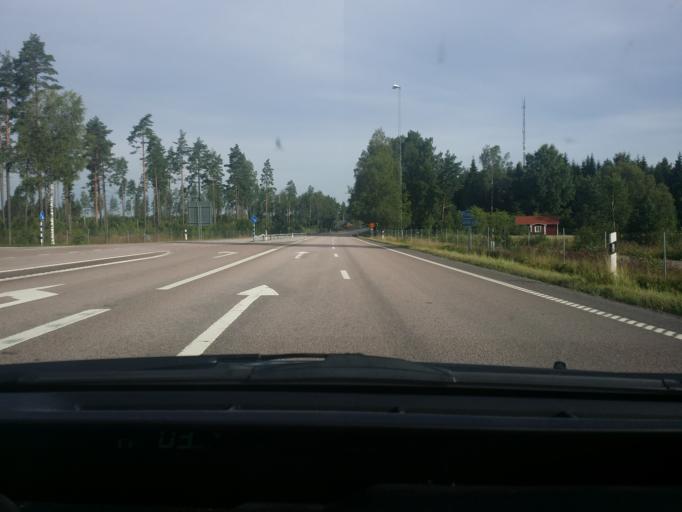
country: SE
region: Vaestmanland
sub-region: Sala Kommun
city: Sala
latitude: 59.8017
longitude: 16.5590
